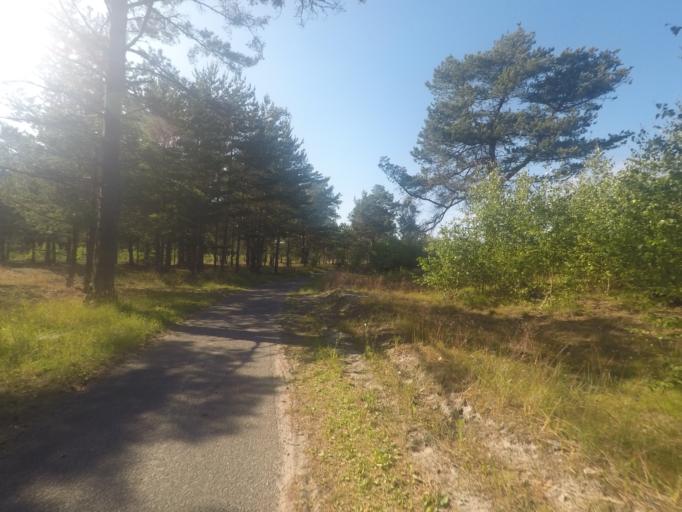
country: LT
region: Klaipedos apskritis
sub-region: Klaipeda
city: Klaipeda
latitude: 55.5832
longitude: 21.1145
